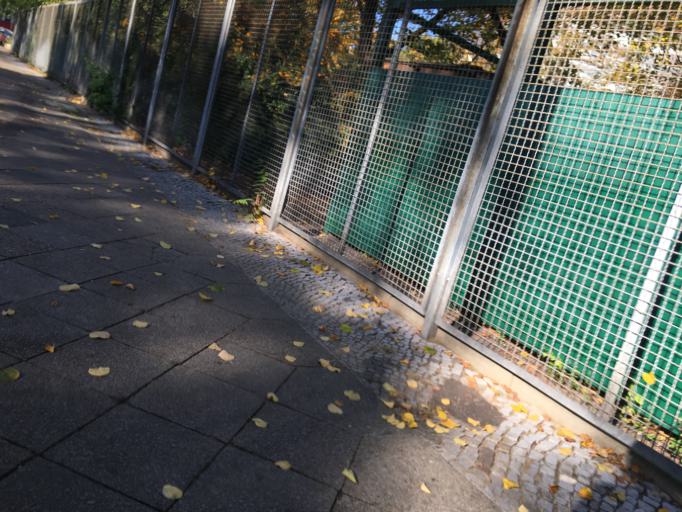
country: DE
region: Berlin
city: Wedding Bezirk
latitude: 52.5466
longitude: 13.3638
